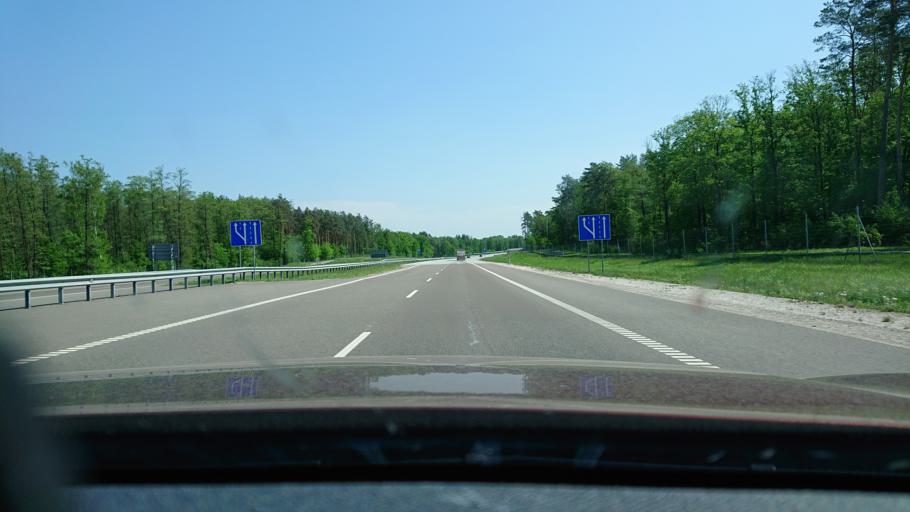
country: PL
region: Subcarpathian Voivodeship
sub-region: Powiat przemyski
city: Stubno
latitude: 49.9592
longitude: 23.0525
